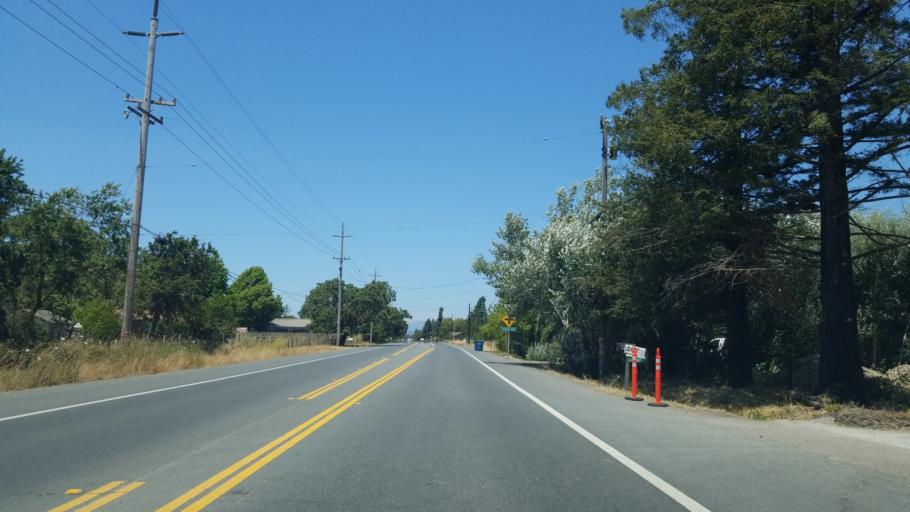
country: US
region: California
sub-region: Sonoma County
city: Roseland
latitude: 38.3736
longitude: -122.7415
